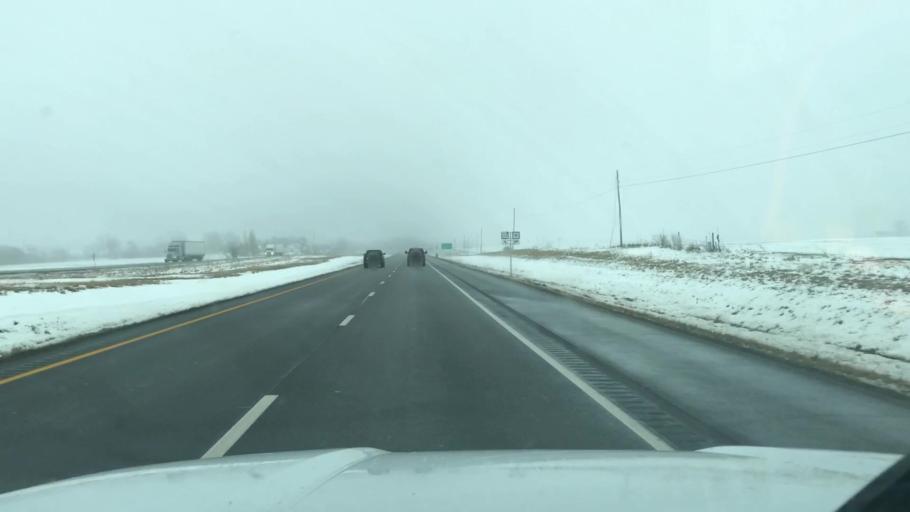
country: US
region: Missouri
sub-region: Clinton County
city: Cameron
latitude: 39.7615
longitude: -94.3643
